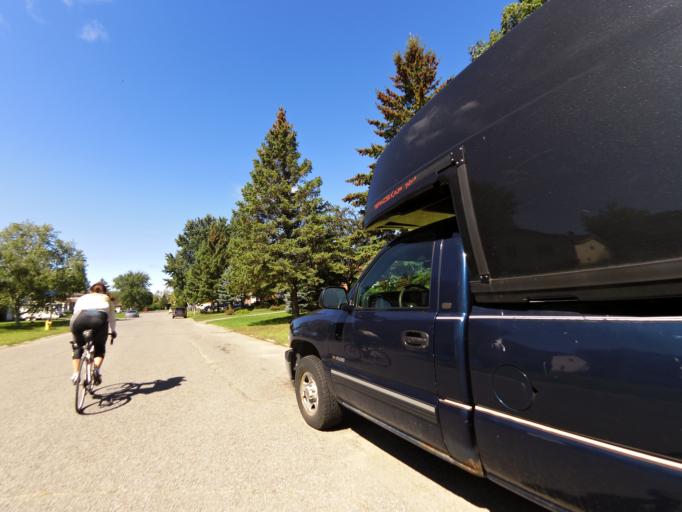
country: CA
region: Ontario
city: Bells Corners
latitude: 45.1923
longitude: -75.8228
